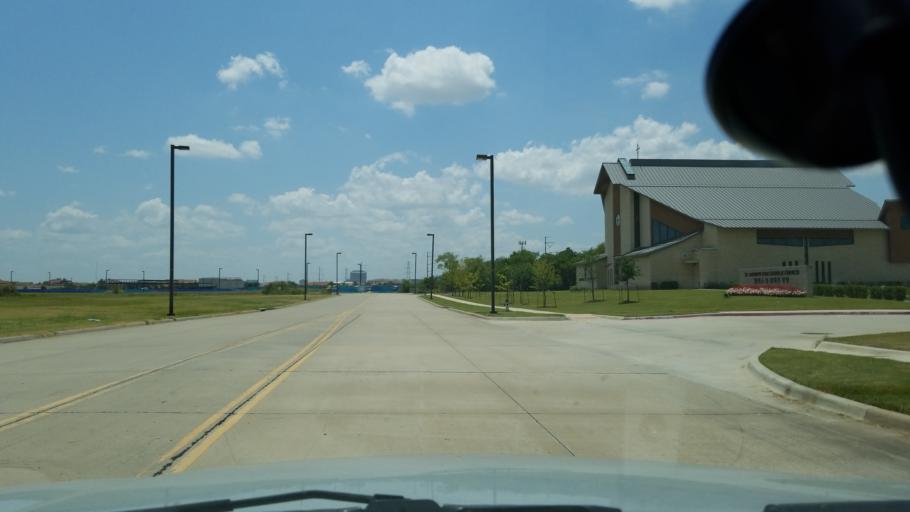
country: US
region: Texas
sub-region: Dallas County
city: Farmers Branch
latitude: 32.9082
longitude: -96.9405
